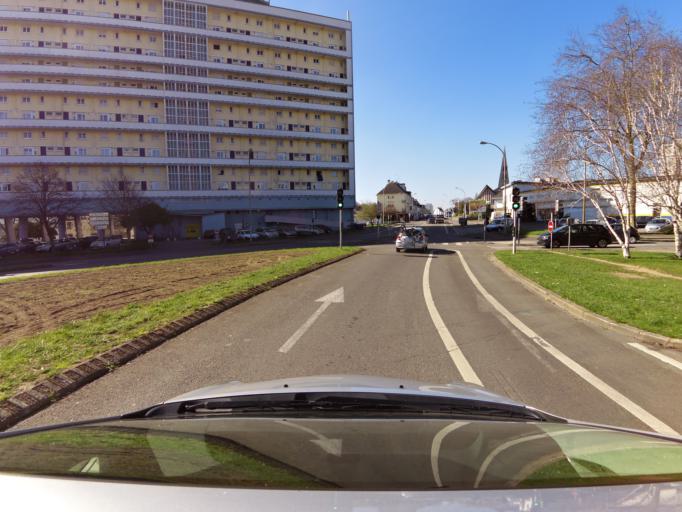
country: FR
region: Brittany
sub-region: Departement du Morbihan
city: Lorient
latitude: 47.7524
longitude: -3.3709
